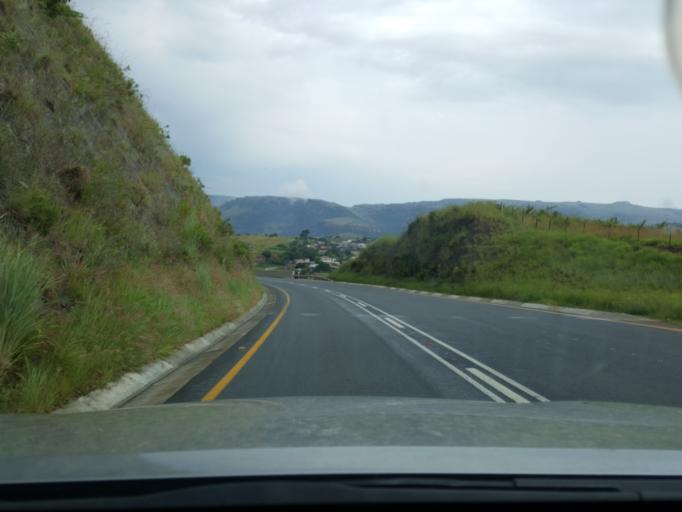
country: ZA
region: Mpumalanga
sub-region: Nkangala District Municipality
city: Belfast
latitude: -25.6331
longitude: 30.3411
